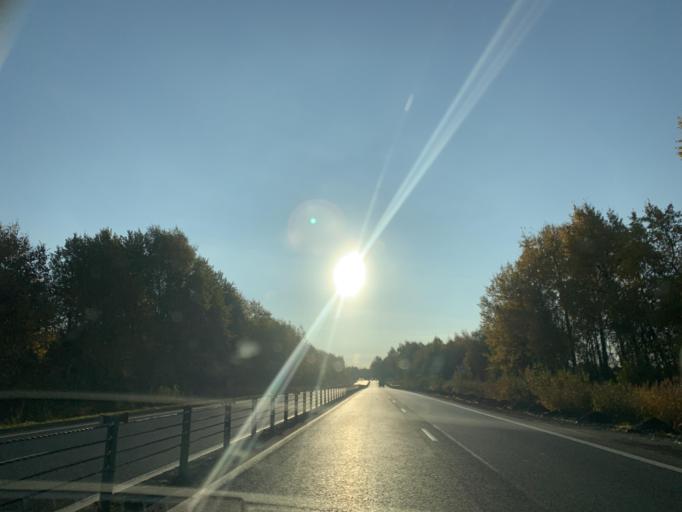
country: RU
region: Jaroslavl
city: Konstantinovskiy
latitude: 57.7819
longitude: 39.6289
